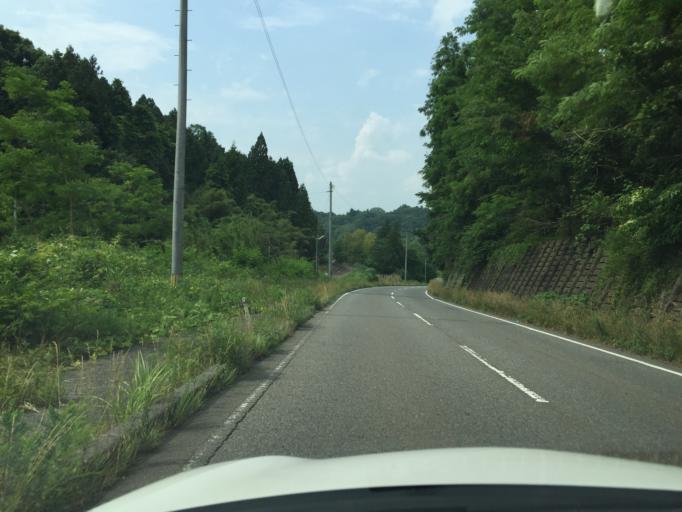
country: JP
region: Fukushima
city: Sukagawa
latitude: 37.3071
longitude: 140.4413
